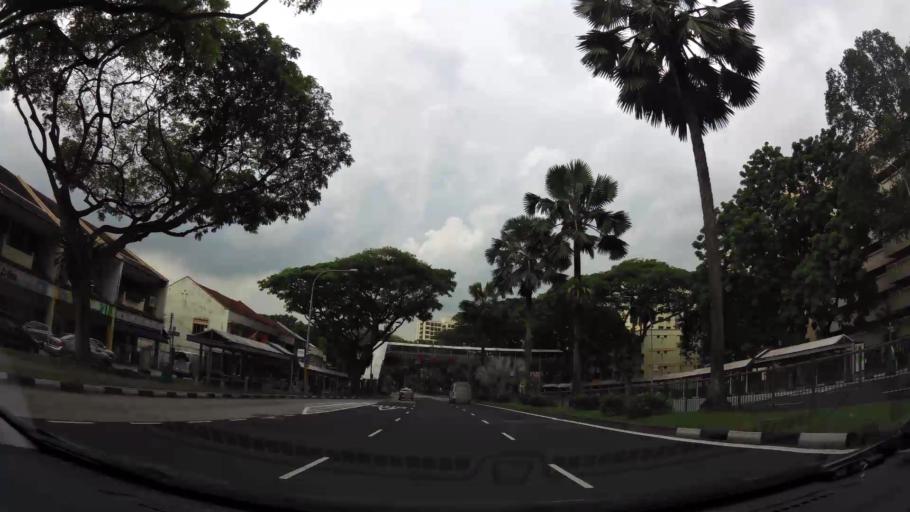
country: MY
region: Johor
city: Kampung Pasir Gudang Baru
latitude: 1.4274
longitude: 103.8266
